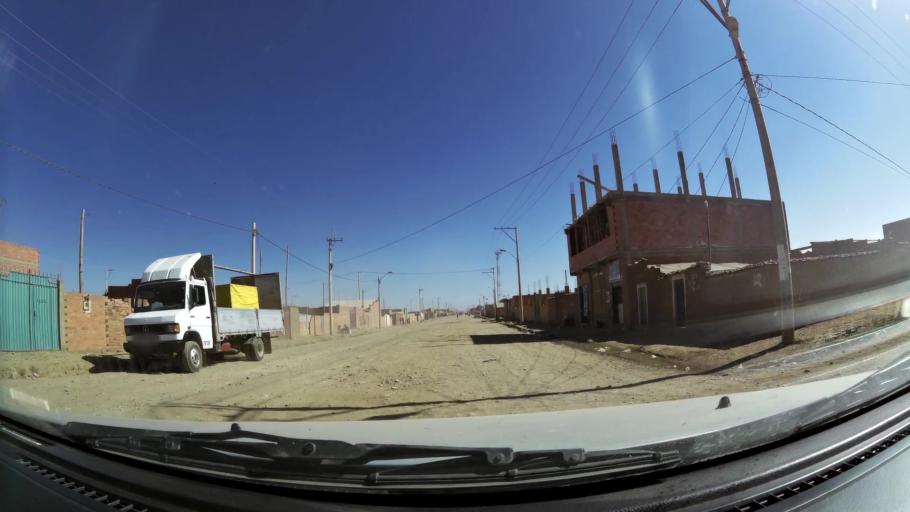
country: BO
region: La Paz
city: La Paz
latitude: -16.6083
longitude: -68.1981
